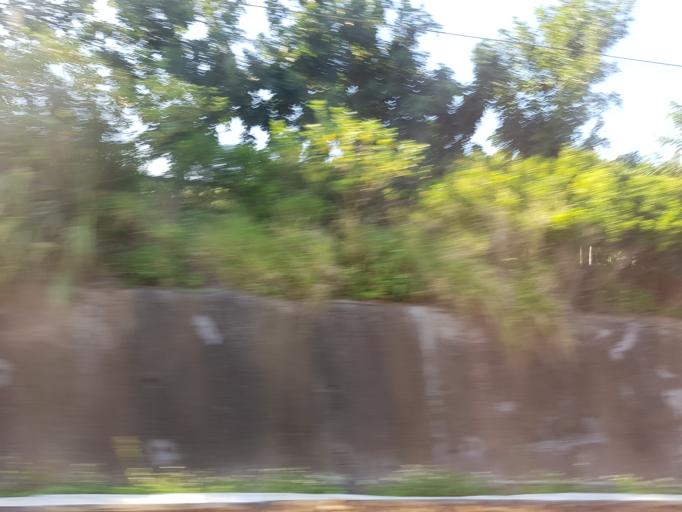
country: TW
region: Taiwan
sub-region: Miaoli
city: Miaoli
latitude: 24.5278
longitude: 120.7949
